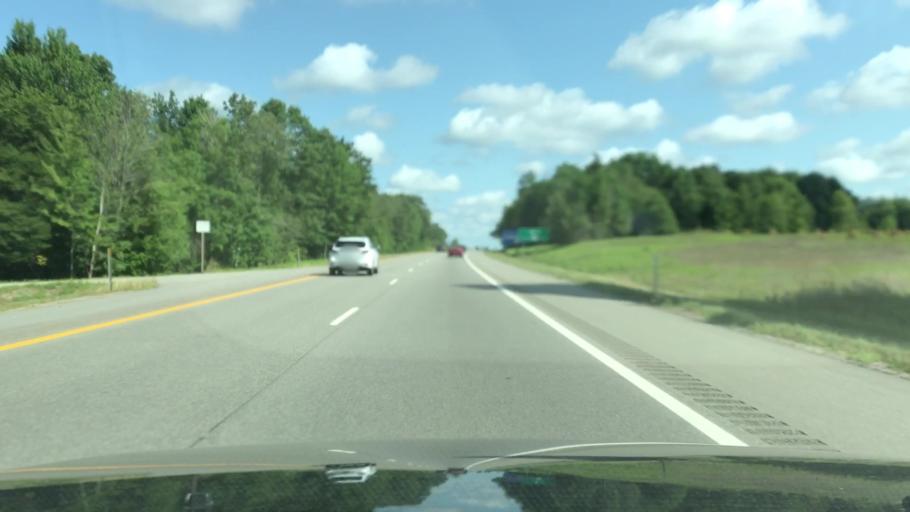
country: US
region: Michigan
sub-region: Mecosta County
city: Big Rapids
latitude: 43.5711
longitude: -85.4908
